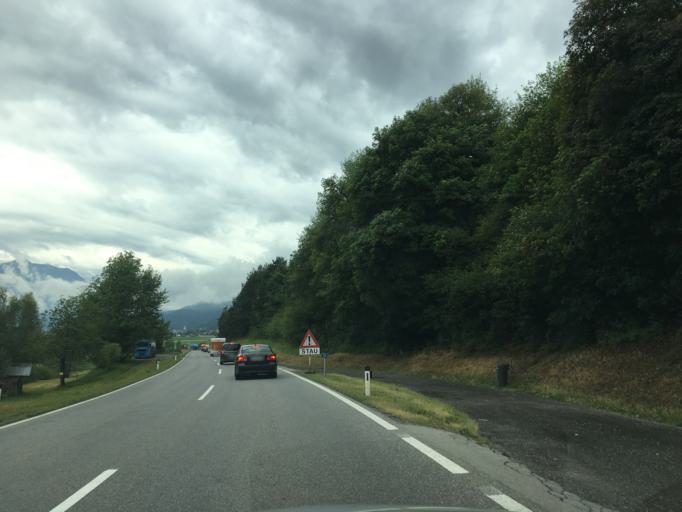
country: AT
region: Tyrol
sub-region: Politischer Bezirk Imst
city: Tarrenz
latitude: 47.2736
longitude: 10.7834
